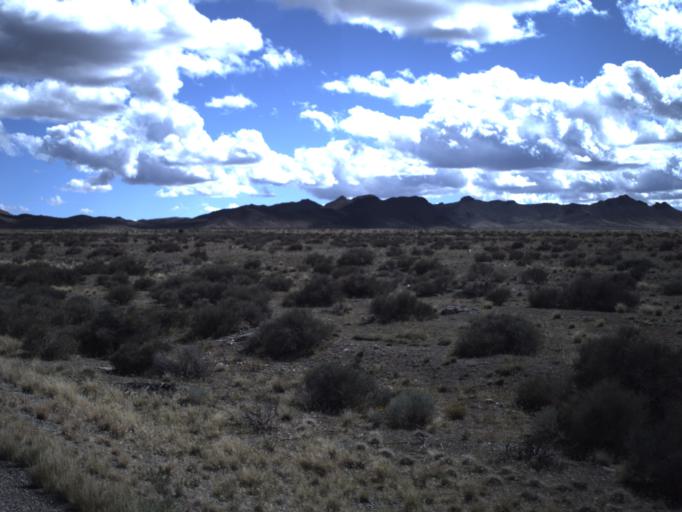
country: US
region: Utah
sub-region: Beaver County
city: Milford
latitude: 38.4480
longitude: -113.3380
